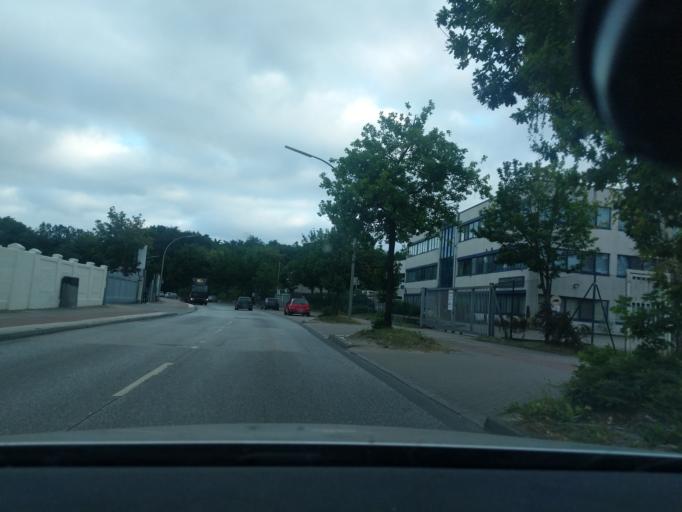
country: DE
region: Hamburg
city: Eidelstedt
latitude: 53.5878
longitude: 9.9072
